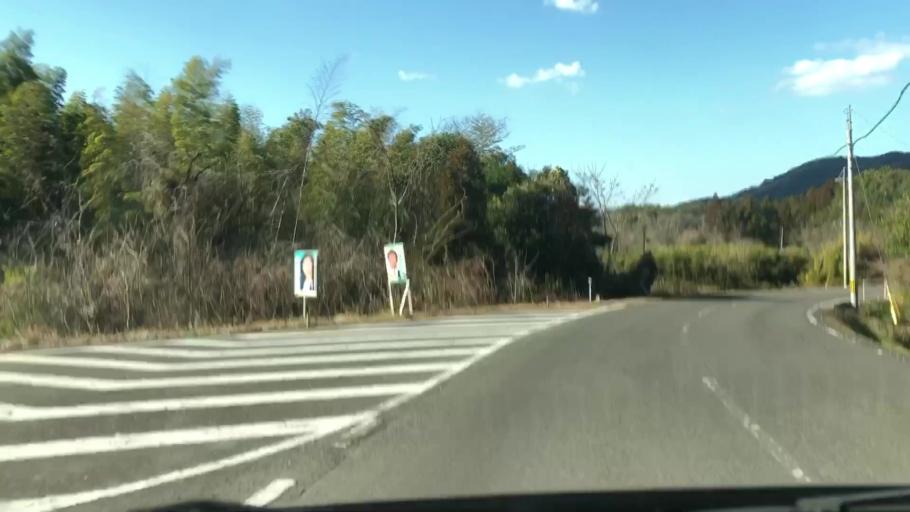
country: JP
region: Kagoshima
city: Satsumasendai
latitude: 31.8552
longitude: 130.3612
